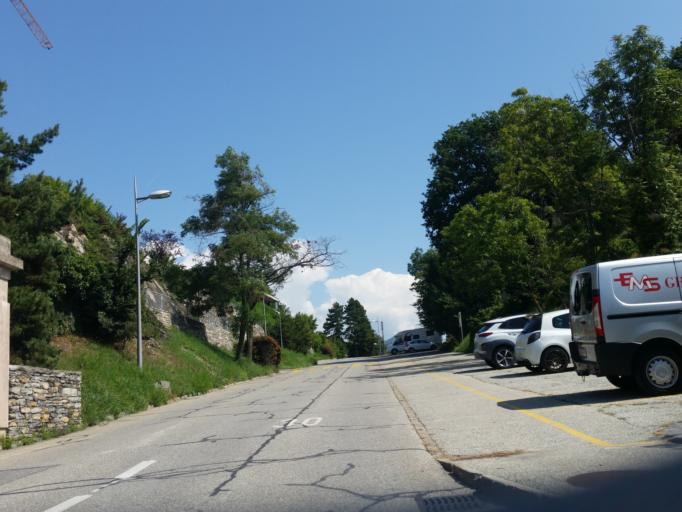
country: CH
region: Valais
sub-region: Sion District
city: Sitten
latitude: 46.2331
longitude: 7.3465
